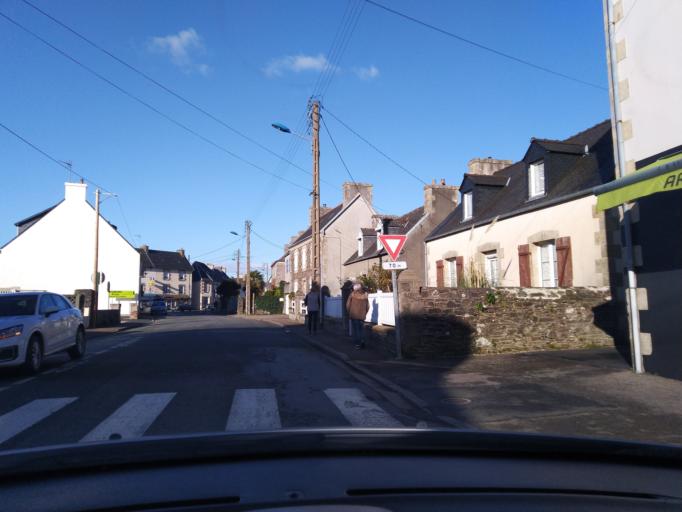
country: FR
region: Brittany
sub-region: Departement des Cotes-d'Armor
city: Plestin-les-Greves
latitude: 48.6605
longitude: -3.6308
